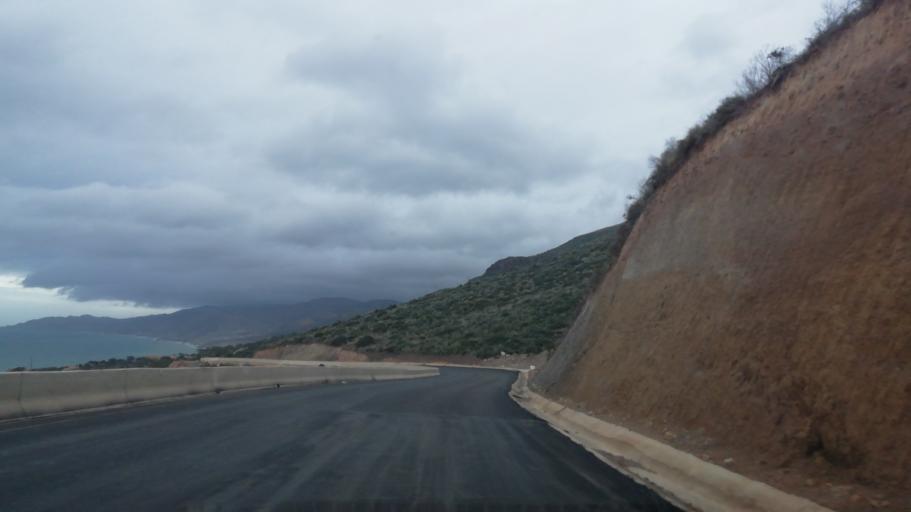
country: DZ
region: Oran
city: Bir el Djir
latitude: 35.7715
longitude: -0.5167
